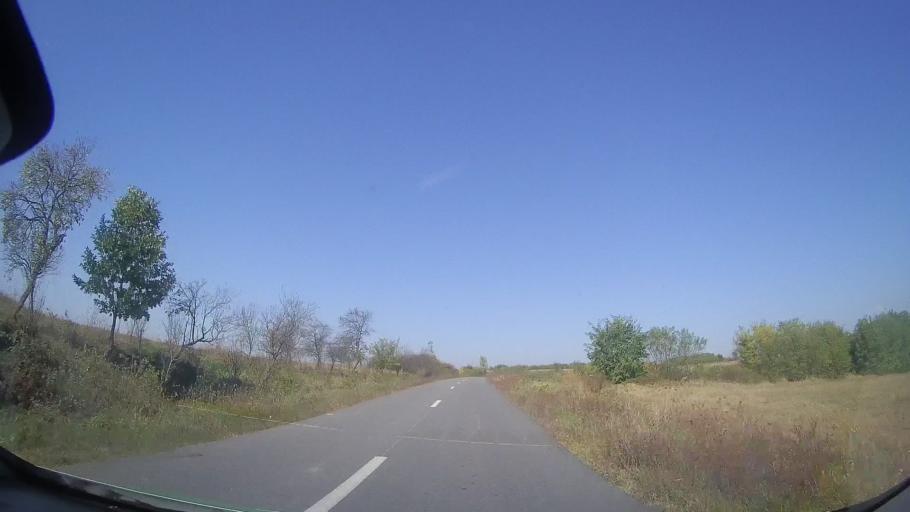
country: RO
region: Timis
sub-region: Comuna Balint
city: Balint
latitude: 45.8217
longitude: 21.8513
